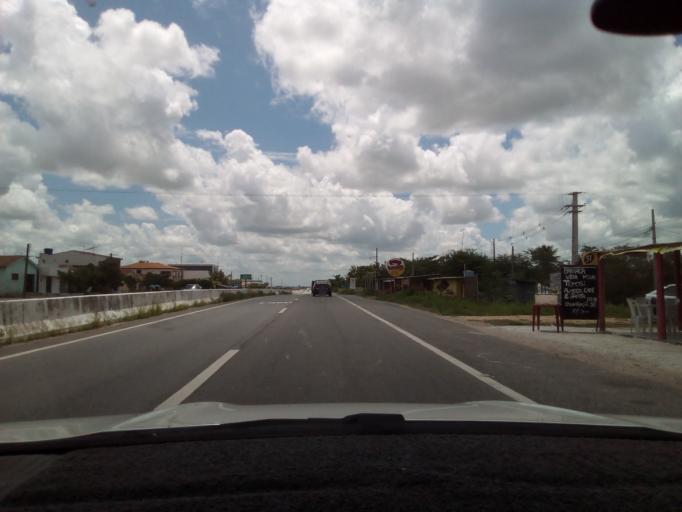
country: BR
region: Paraiba
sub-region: Gurinhem
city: Gurinhem
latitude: -7.1733
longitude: -35.3947
